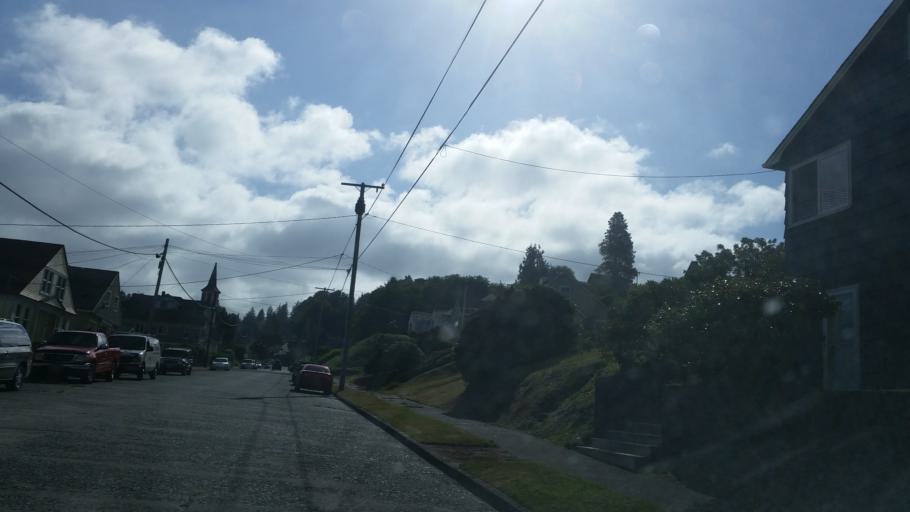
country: US
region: Oregon
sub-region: Clatsop County
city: Astoria
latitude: 46.1914
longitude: -123.8073
